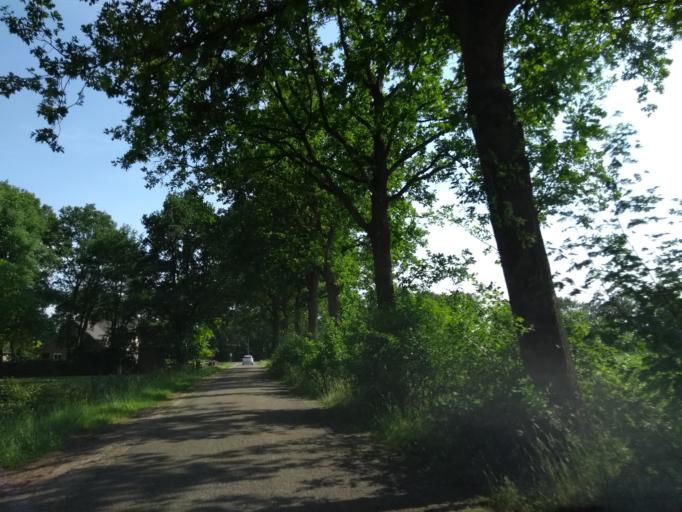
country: DE
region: Lower Saxony
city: Nordhorn
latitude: 52.3704
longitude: 7.0332
